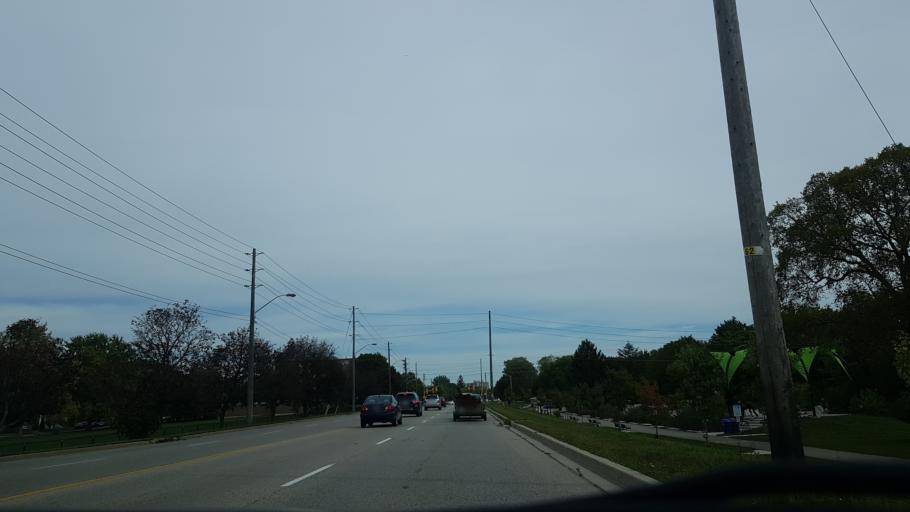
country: CA
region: Ontario
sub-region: Wellington County
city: Guelph
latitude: 43.5325
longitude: -80.2564
